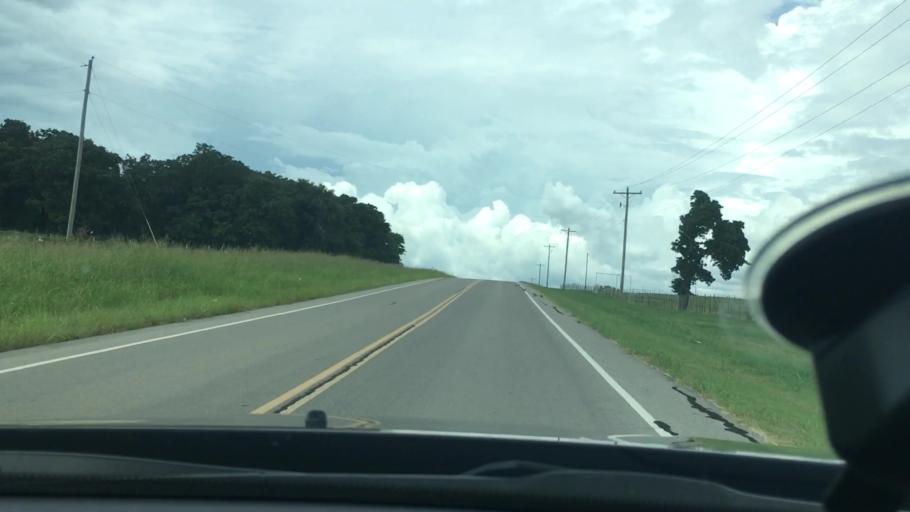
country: US
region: Oklahoma
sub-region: Garvin County
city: Stratford
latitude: 34.8091
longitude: -97.0554
